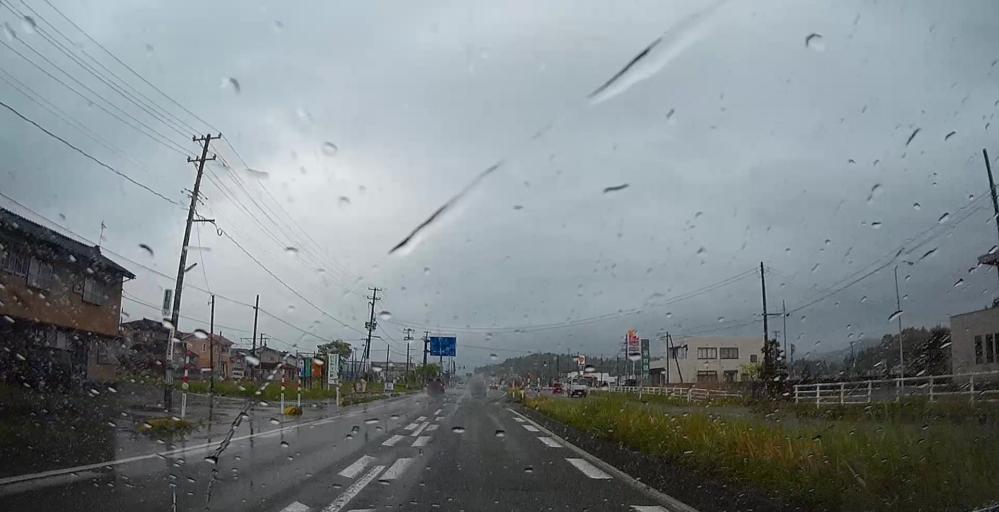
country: JP
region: Niigata
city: Kashiwazaki
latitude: 37.4469
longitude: 138.6397
